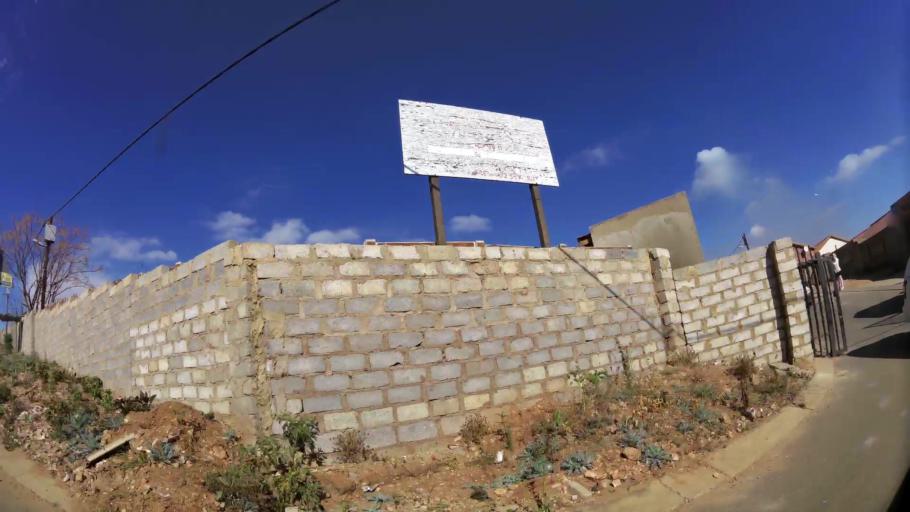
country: ZA
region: Gauteng
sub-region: City of Tshwane Metropolitan Municipality
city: Cullinan
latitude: -25.6910
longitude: 28.4157
